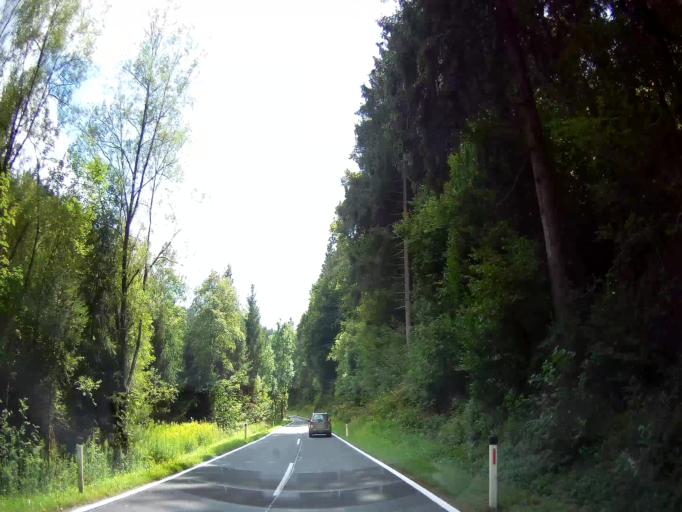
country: AT
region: Carinthia
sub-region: Politischer Bezirk Spittal an der Drau
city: Trebesing
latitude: 46.8685
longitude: 13.5065
